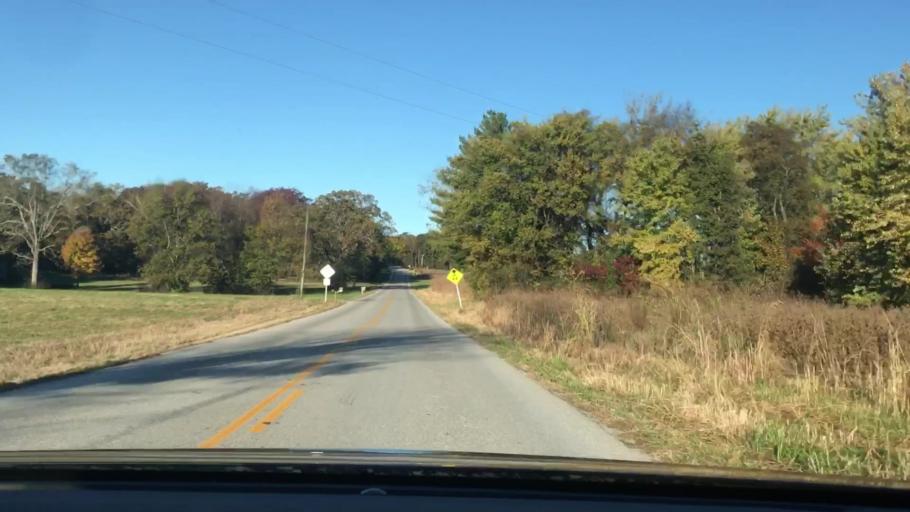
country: US
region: Kentucky
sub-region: Logan County
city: Auburn
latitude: 36.8186
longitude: -86.6475
